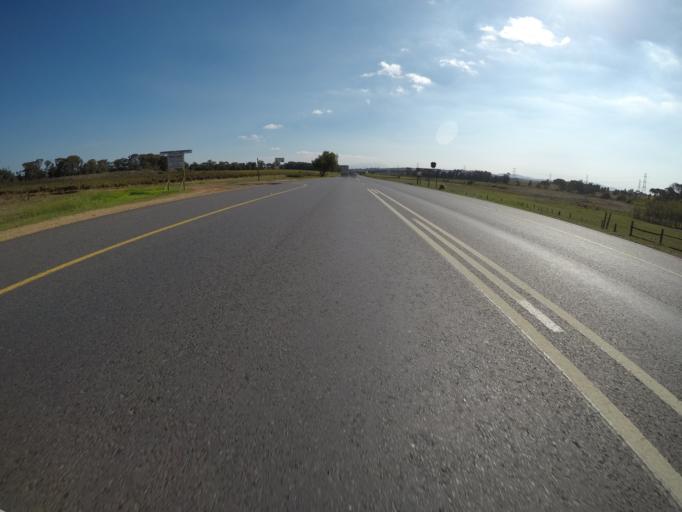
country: ZA
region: Western Cape
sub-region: City of Cape Town
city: Kraaifontein
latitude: -33.8803
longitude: 18.7635
